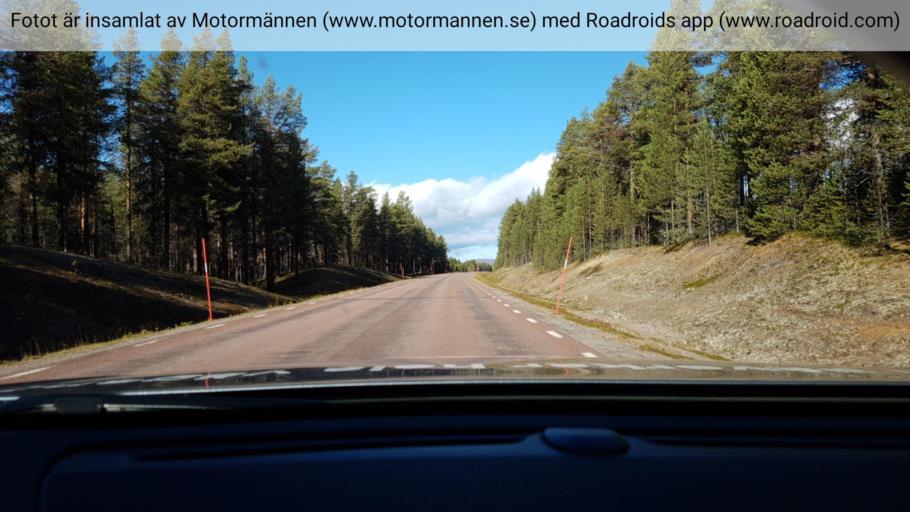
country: SE
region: Norrbotten
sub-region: Arjeplogs Kommun
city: Arjeplog
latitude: 66.0200
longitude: 18.0736
